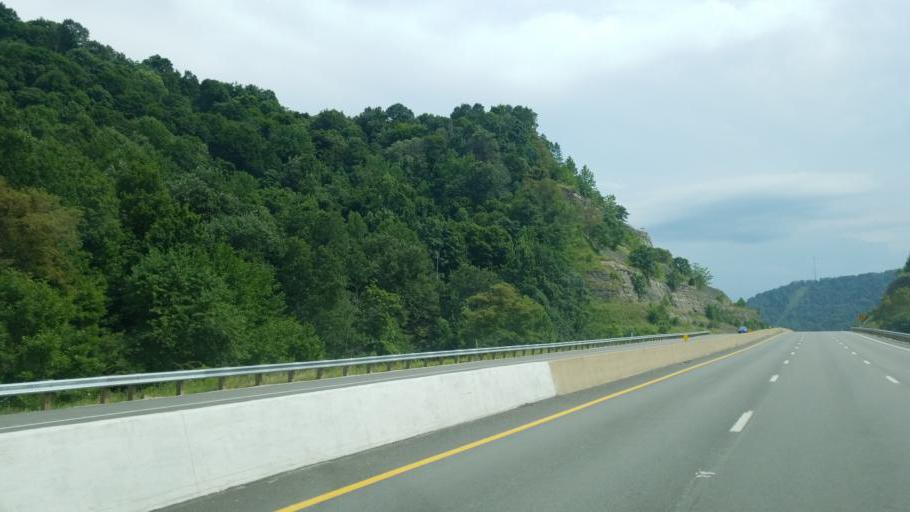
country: US
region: West Virginia
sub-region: Logan County
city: Chapmanville
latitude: 37.9125
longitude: -82.0378
